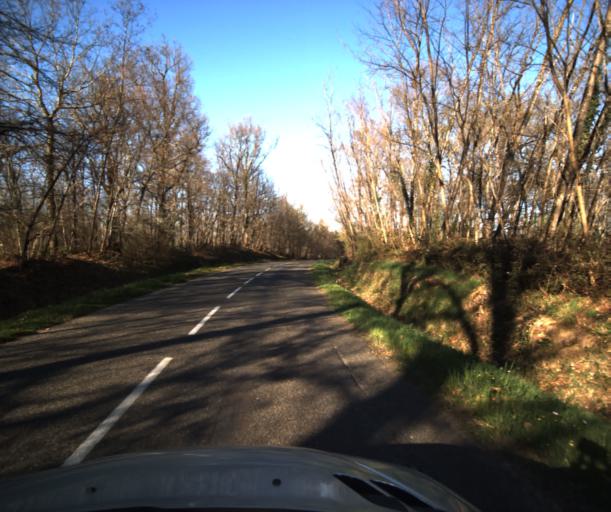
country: FR
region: Midi-Pyrenees
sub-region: Departement du Tarn-et-Garonne
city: Campsas
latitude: 43.9321
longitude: 1.2950
